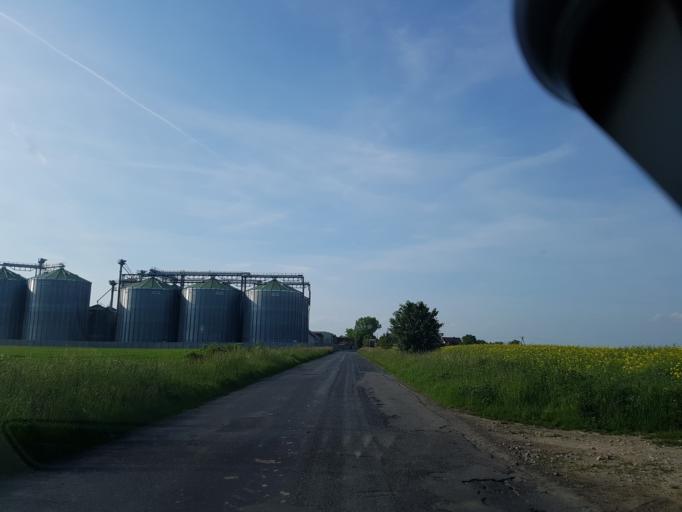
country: PL
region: Lower Silesian Voivodeship
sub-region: Powiat strzelinski
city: Wiazow
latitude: 50.8487
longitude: 17.1866
